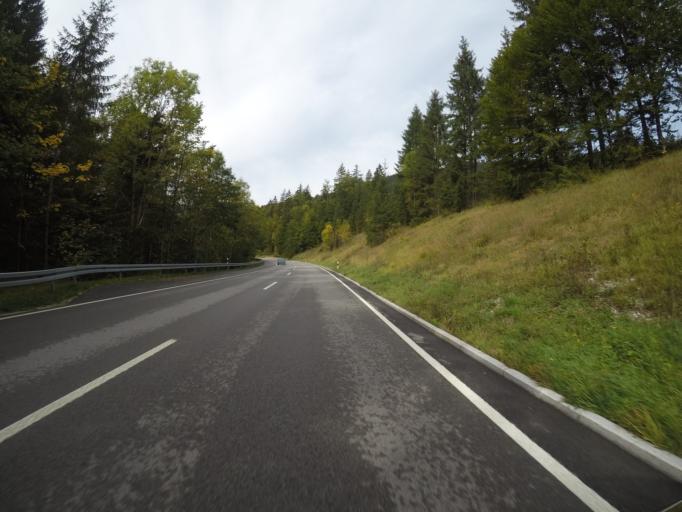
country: DE
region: Bavaria
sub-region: Upper Bavaria
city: Lenggries
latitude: 47.5829
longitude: 11.5938
